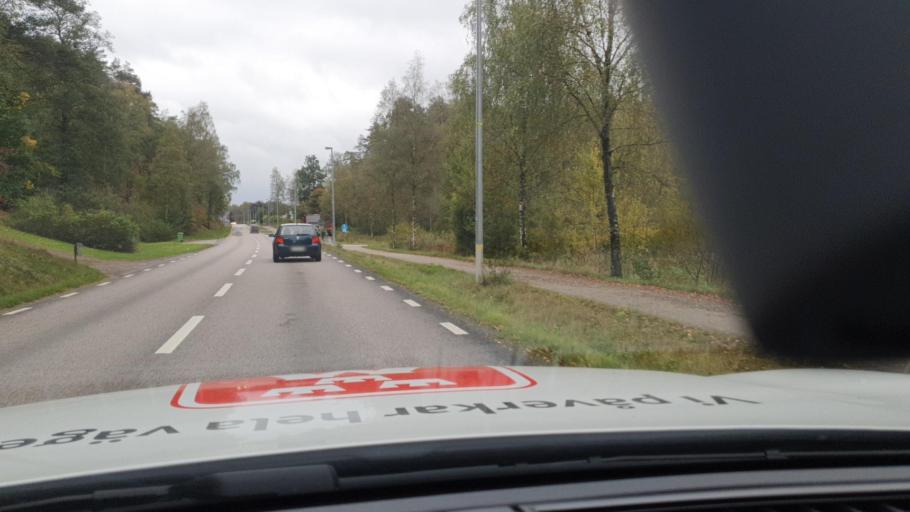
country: SE
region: Halland
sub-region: Halmstads Kommun
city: Getinge
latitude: 57.1330
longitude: 12.7183
